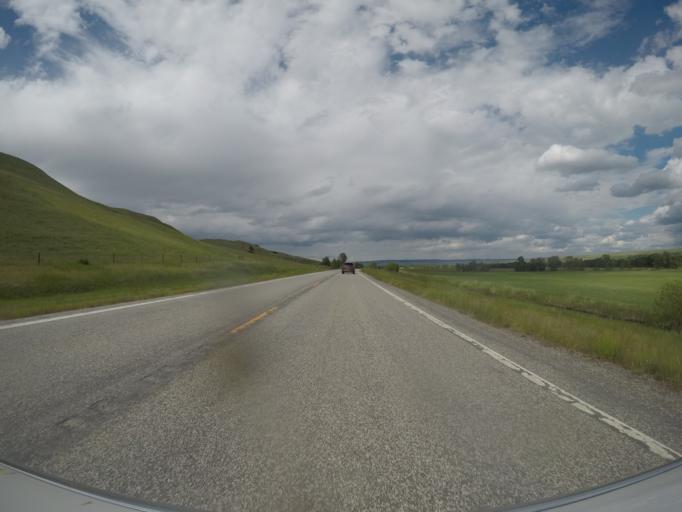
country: US
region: Montana
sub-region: Sweet Grass County
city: Big Timber
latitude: 45.8053
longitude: -109.9657
